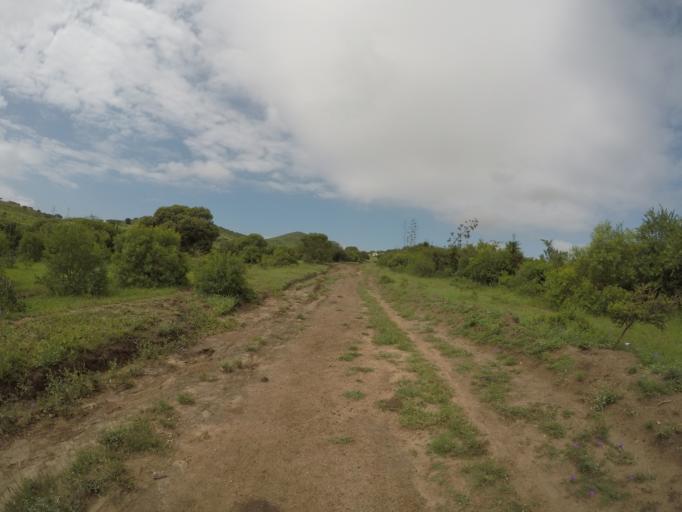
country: ZA
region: KwaZulu-Natal
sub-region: uThungulu District Municipality
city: Empangeni
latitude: -28.6237
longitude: 31.8650
